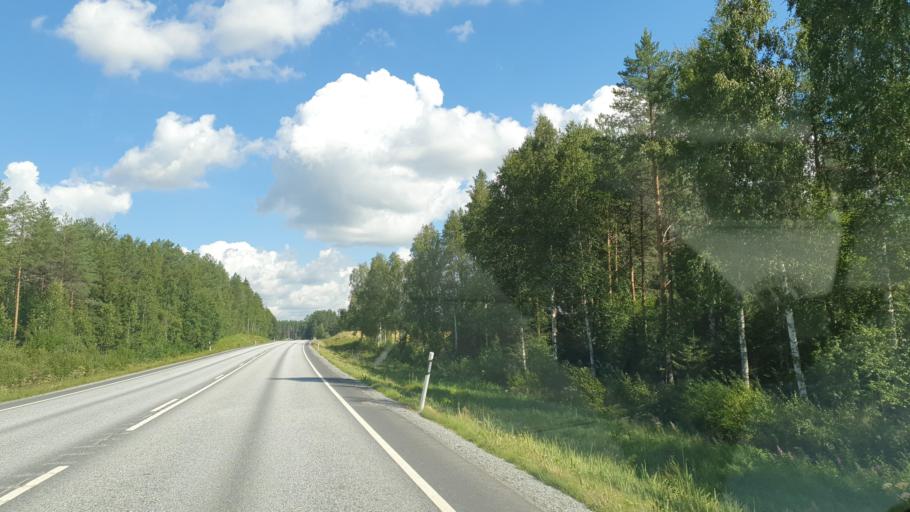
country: FI
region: Northern Savo
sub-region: Ylae-Savo
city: Sonkajaervi
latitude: 63.8390
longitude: 27.4273
